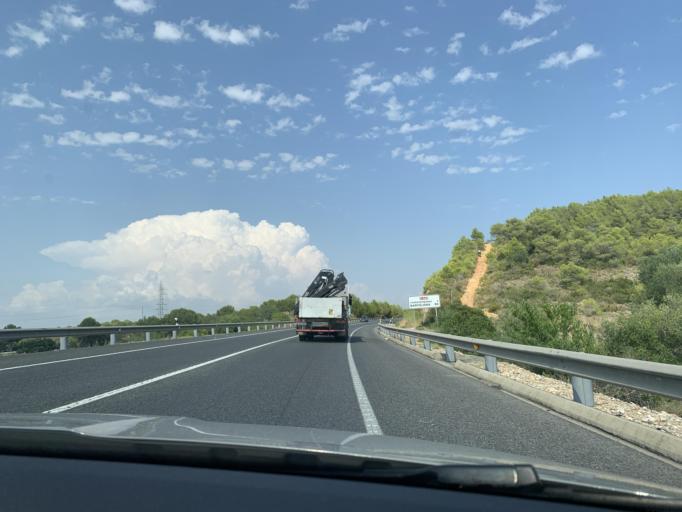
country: ES
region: Catalonia
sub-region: Provincia de Tarragona
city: Altafulla
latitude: 41.1540
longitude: 1.3681
